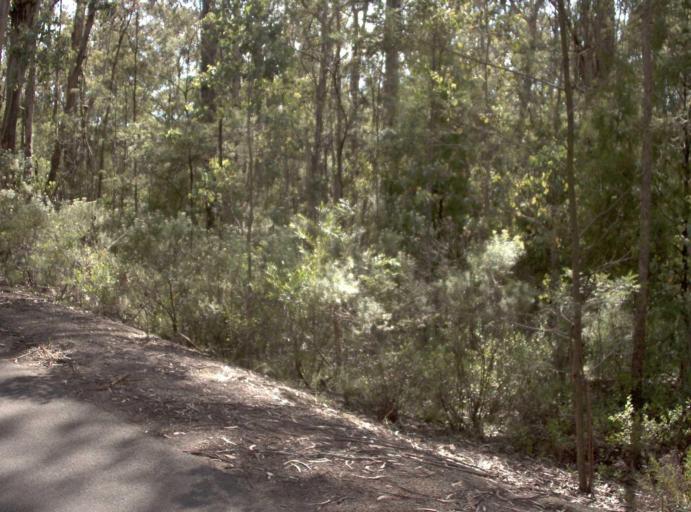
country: AU
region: Victoria
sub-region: East Gippsland
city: Lakes Entrance
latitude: -37.4240
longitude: 148.1280
